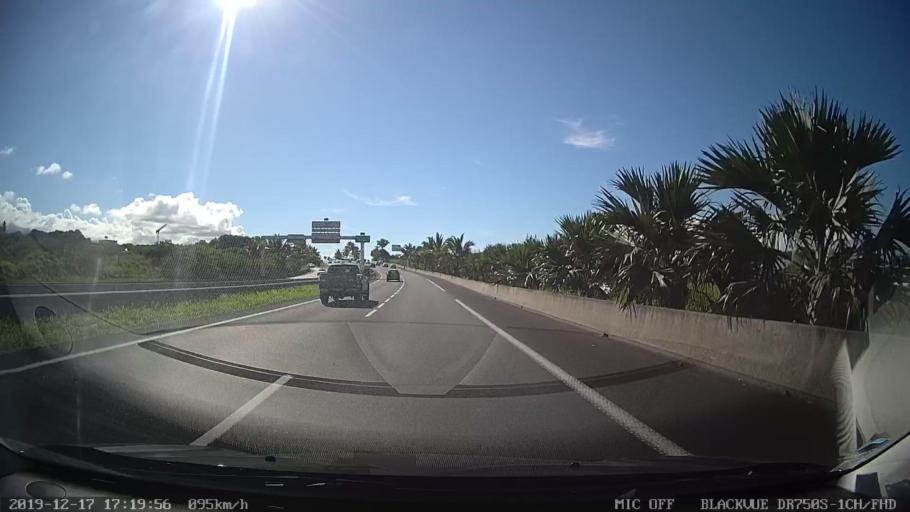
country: RE
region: Reunion
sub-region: Reunion
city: Saint-Pierre
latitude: -21.3300
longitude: 55.4537
